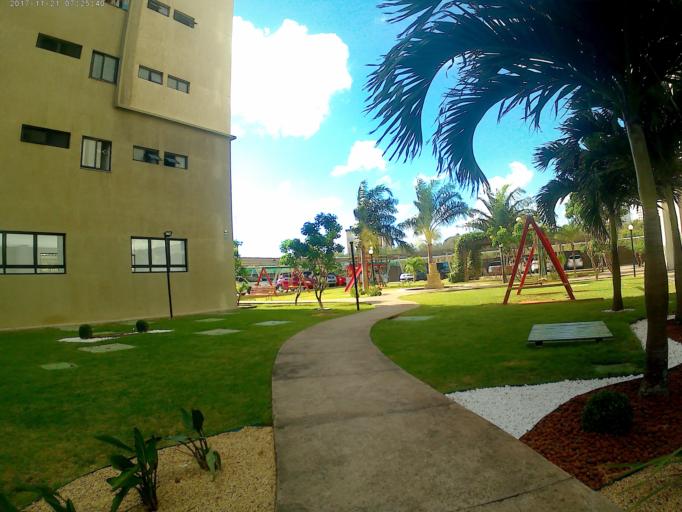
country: BR
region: Rio Grande do Norte
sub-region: Natal
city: Natal
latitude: -5.8637
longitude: -35.2130
